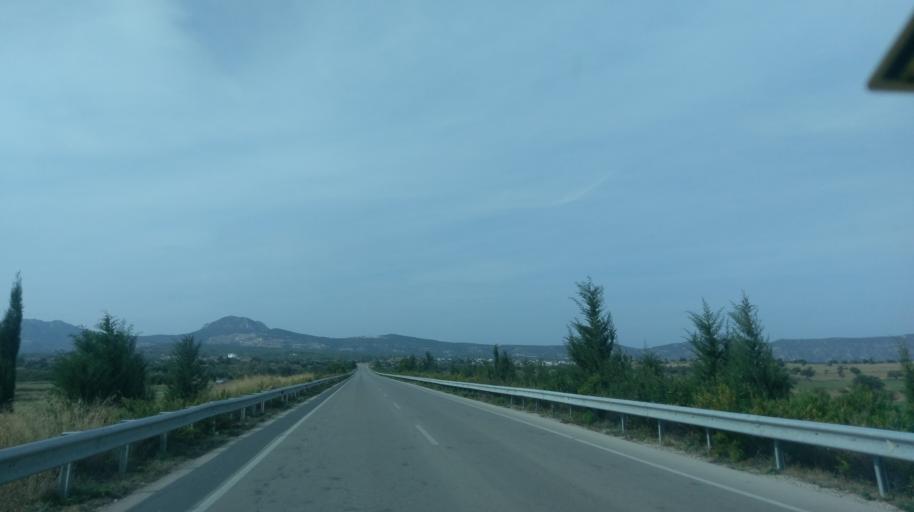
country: CY
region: Ammochostos
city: Leonarisso
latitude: 35.3941
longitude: 34.0061
